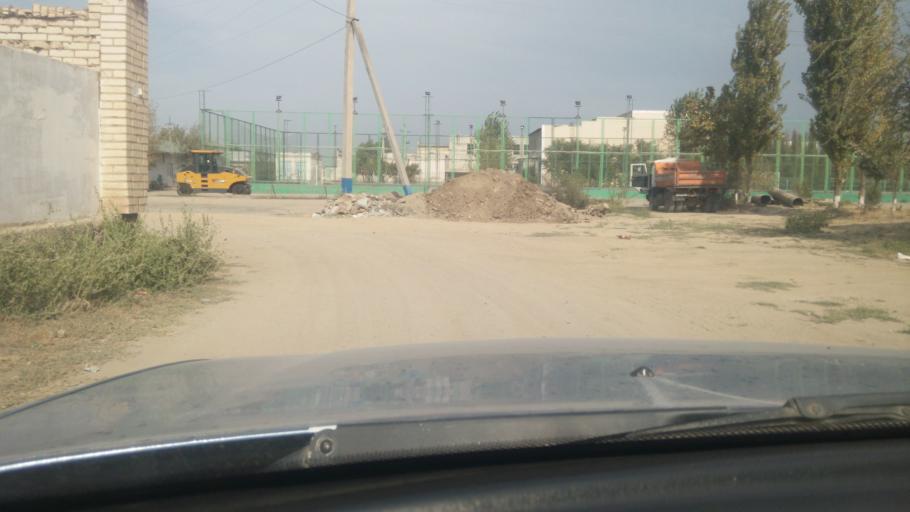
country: UZ
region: Sirdaryo
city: Guliston
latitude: 40.5149
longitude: 68.7837
